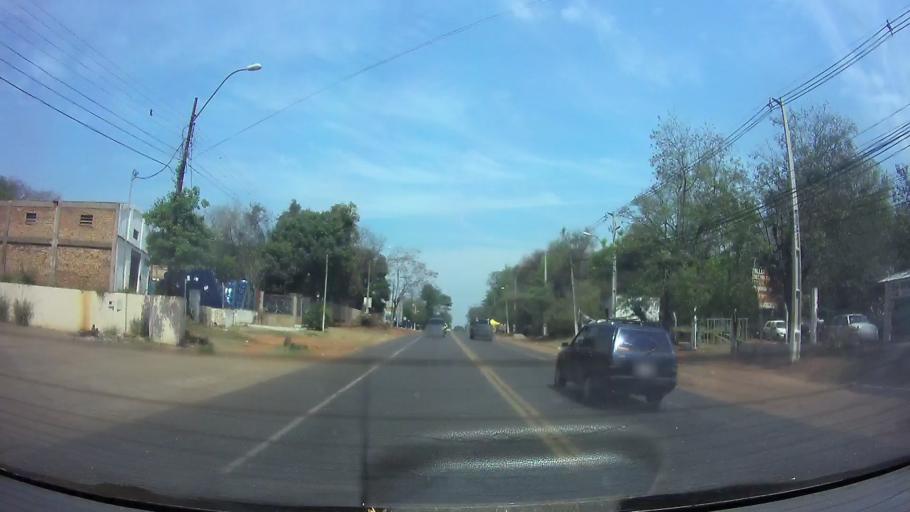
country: PY
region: Central
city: Capiata
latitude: -25.3798
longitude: -57.4748
